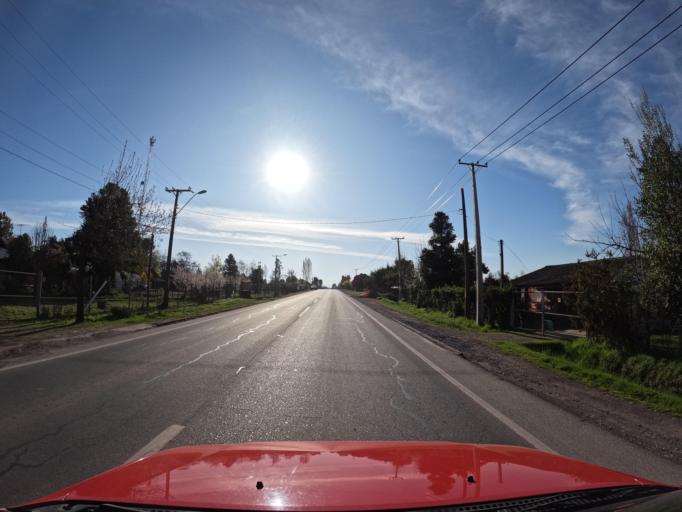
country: CL
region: Maule
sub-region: Provincia de Curico
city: Teno
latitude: -34.9500
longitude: -70.9880
